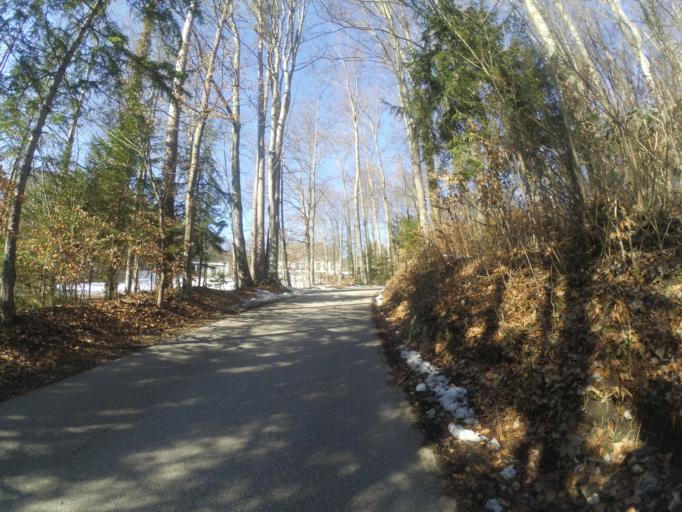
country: DE
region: Bavaria
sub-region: Upper Bavaria
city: Feldkirchen-Westerham
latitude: 47.9068
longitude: 11.8319
